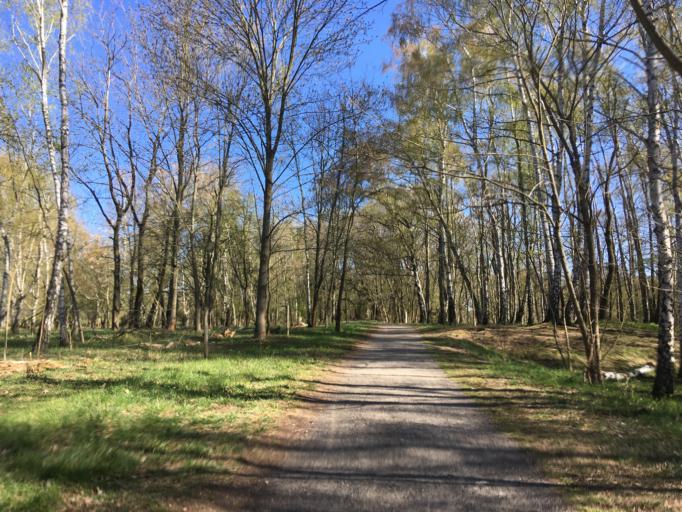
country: DE
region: Berlin
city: Buch
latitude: 52.6376
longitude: 13.4652
